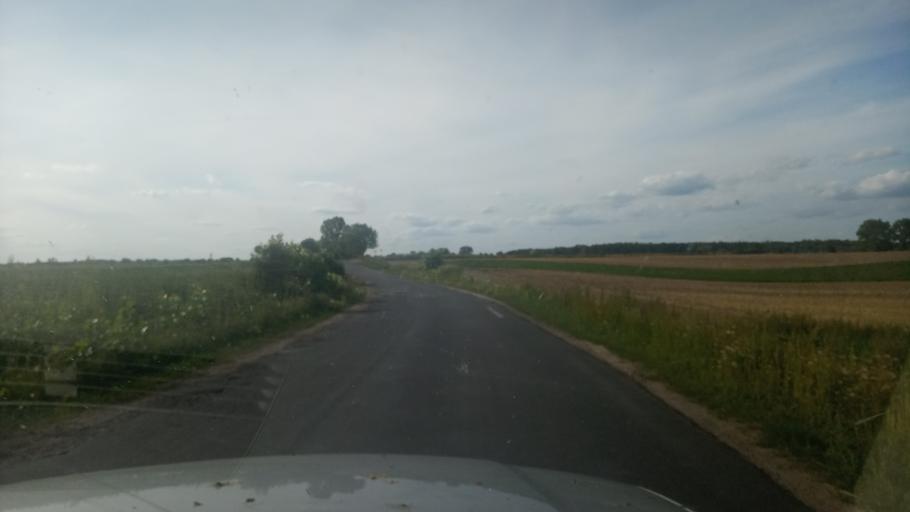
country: PL
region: Kujawsko-Pomorskie
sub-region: Powiat nakielski
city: Sadki
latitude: 53.1993
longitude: 17.3831
